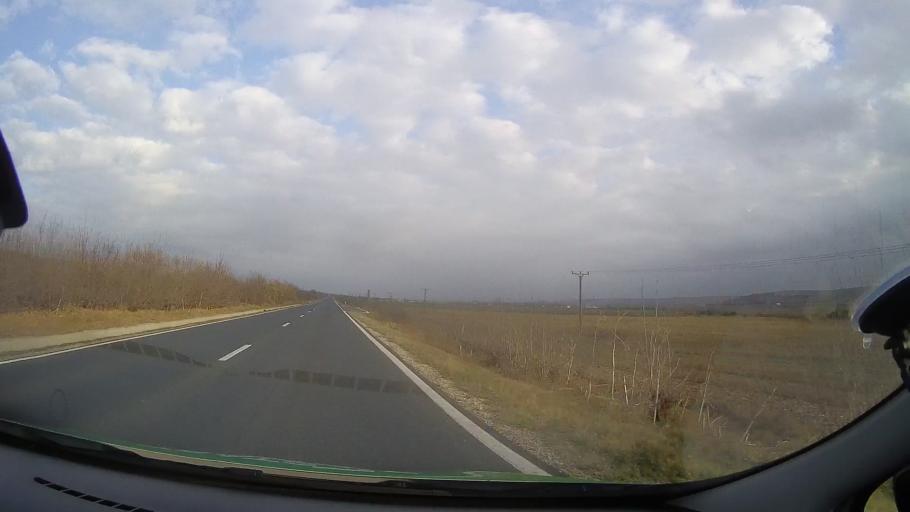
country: RO
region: Constanta
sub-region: Comuna Mircea Voda
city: Satu Nou
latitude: 44.2707
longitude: 28.2026
